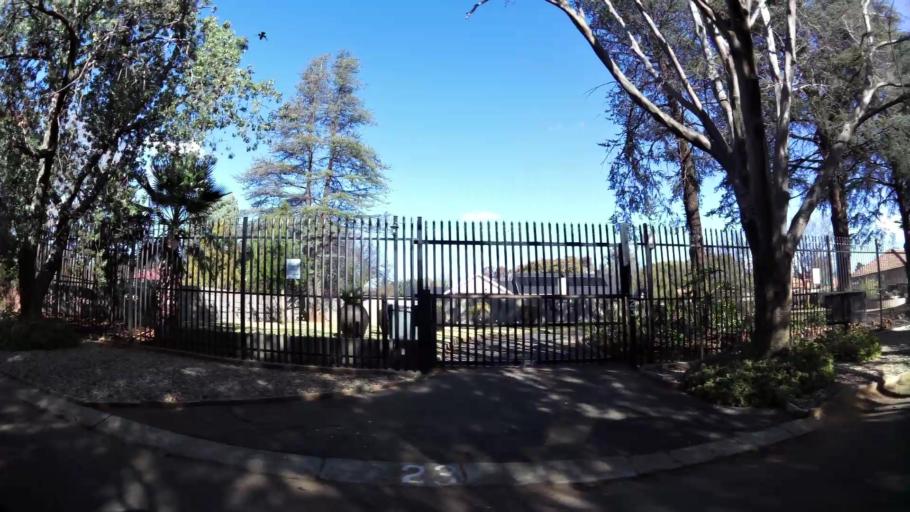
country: ZA
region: Gauteng
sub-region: West Rand District Municipality
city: Carletonville
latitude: -26.3705
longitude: 27.4071
